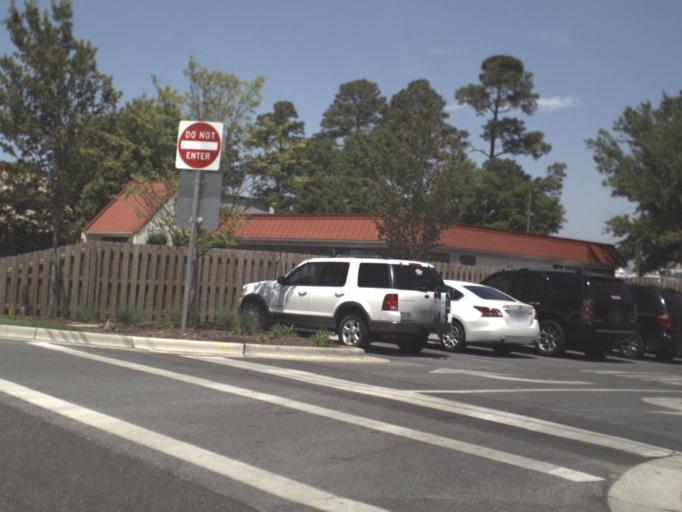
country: US
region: Florida
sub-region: Escambia County
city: Ferry Pass
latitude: 30.4821
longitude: -87.2107
